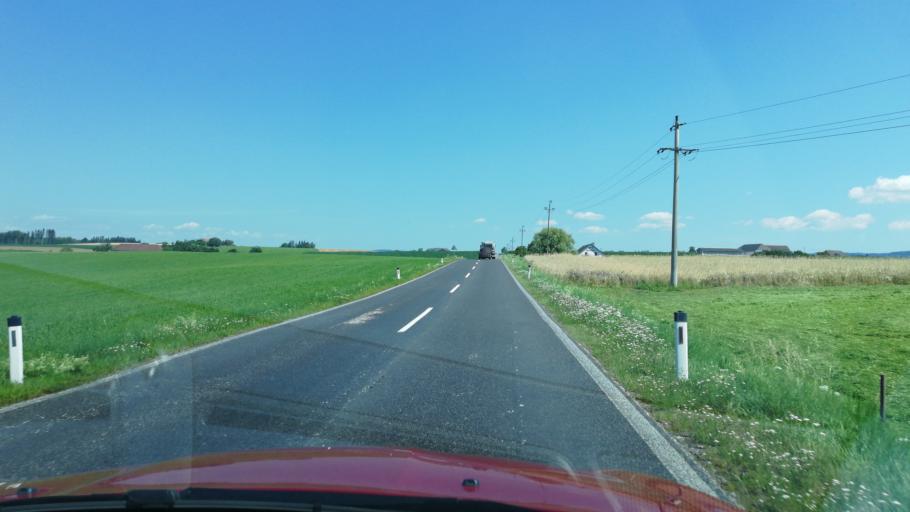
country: AT
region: Upper Austria
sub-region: Politischer Bezirk Urfahr-Umgebung
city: Herzogsdorf
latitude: 48.4456
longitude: 14.0537
